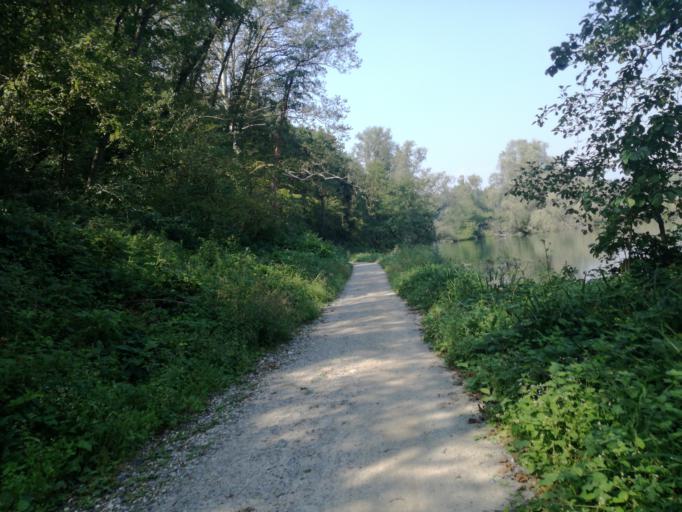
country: IT
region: Lombardy
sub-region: Provincia di Lecco
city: Arlate
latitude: 45.7249
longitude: 9.4475
